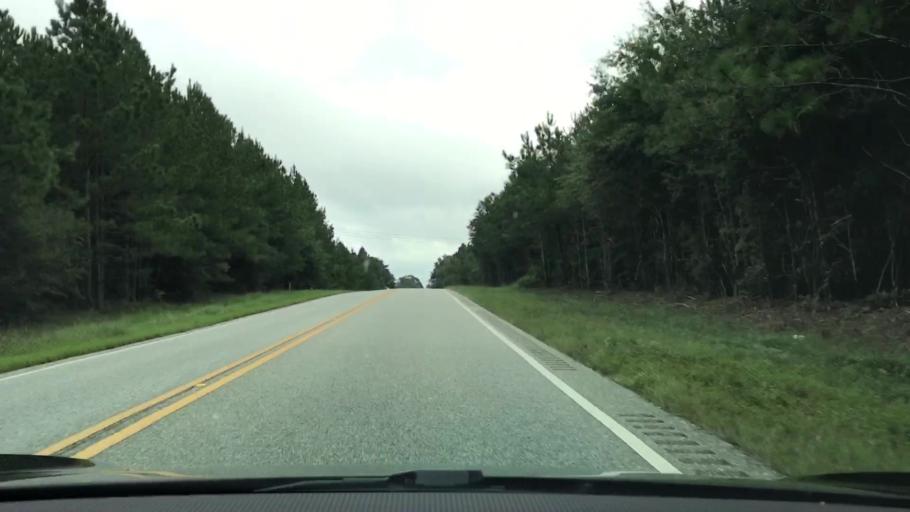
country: US
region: Alabama
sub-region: Geneva County
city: Samson
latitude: 31.0220
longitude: -86.1215
